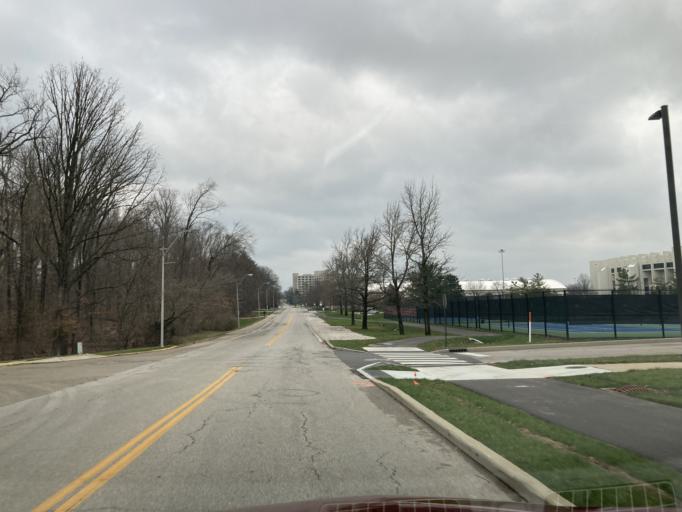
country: US
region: Indiana
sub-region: Monroe County
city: Bloomington
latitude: 39.1841
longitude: -86.5192
